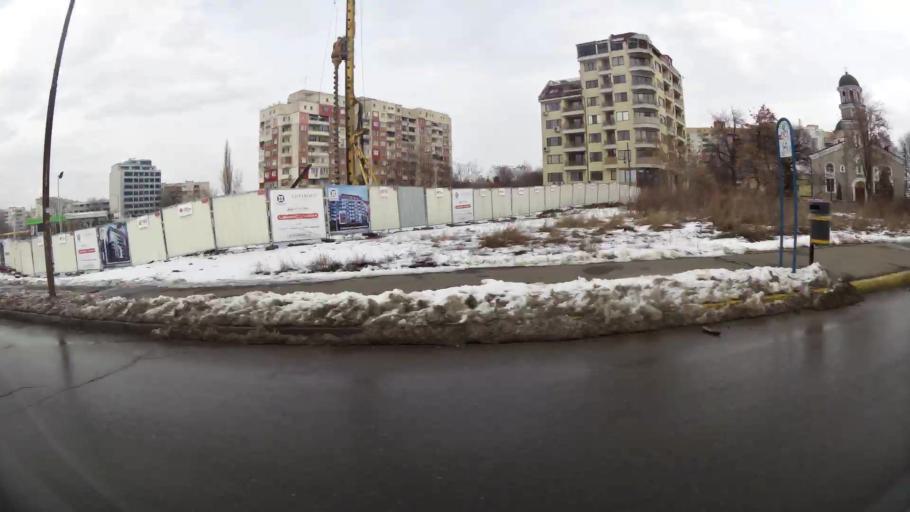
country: BG
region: Sofia-Capital
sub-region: Stolichna Obshtina
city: Sofia
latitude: 42.7008
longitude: 23.3514
